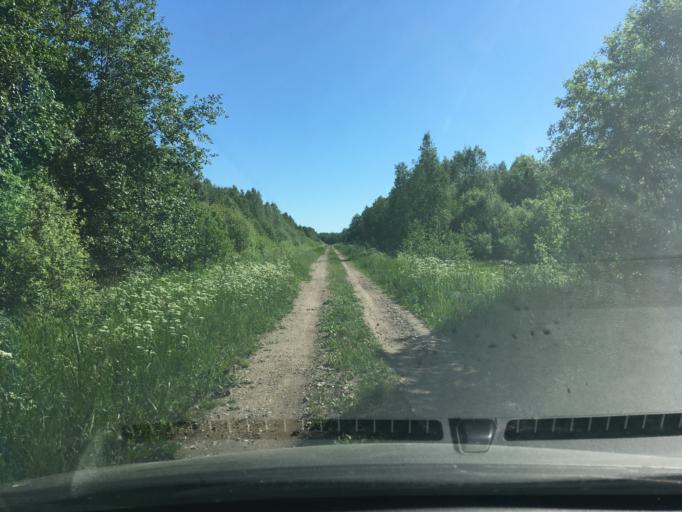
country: EE
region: Laeaene
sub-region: Lihula vald
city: Lihula
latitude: 58.6277
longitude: 23.7298
